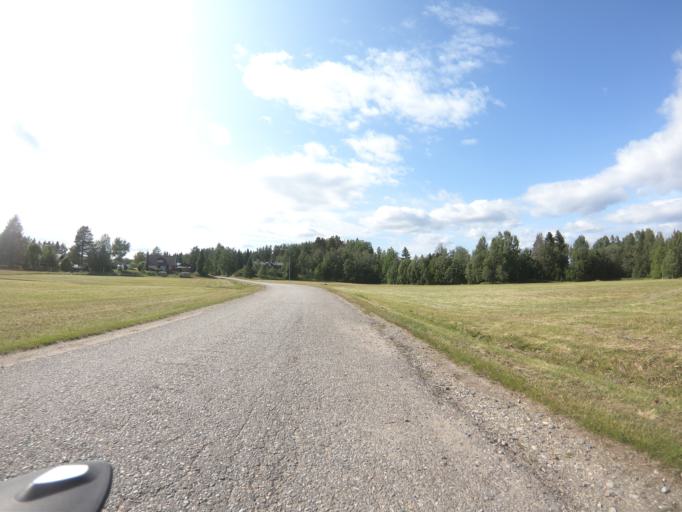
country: SE
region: Vaesterbotten
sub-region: Umea Kommun
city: Roback
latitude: 63.8321
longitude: 20.1189
